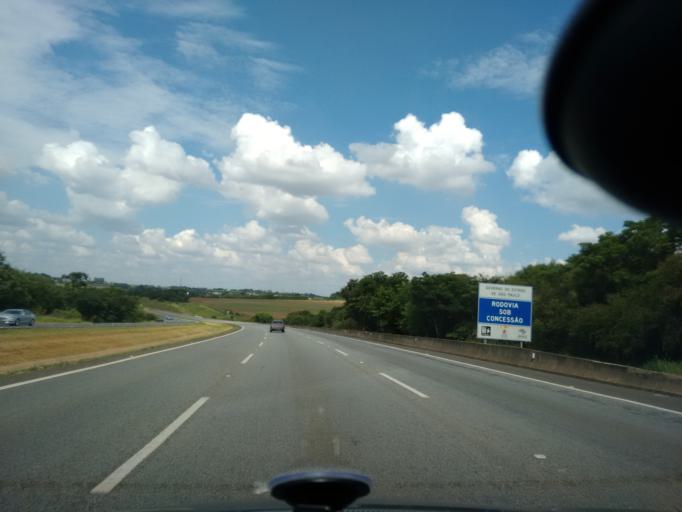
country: BR
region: Sao Paulo
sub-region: Sumare
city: Sumare
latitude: -22.8706
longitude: -47.2752
